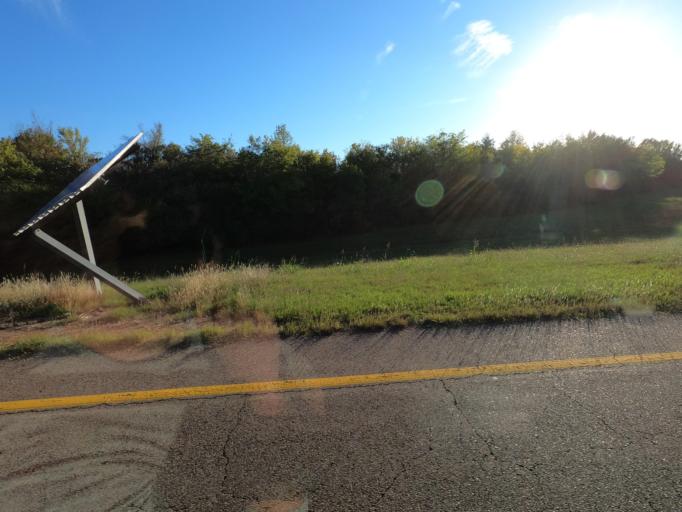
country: US
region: Tennessee
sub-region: Shelby County
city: Millington
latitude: 35.3317
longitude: -89.9189
